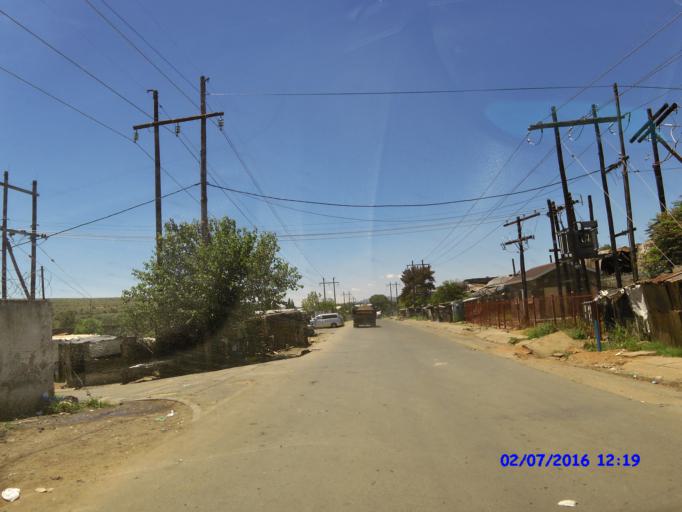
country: LS
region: Maseru
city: Maseru
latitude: -29.2969
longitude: 27.4683
